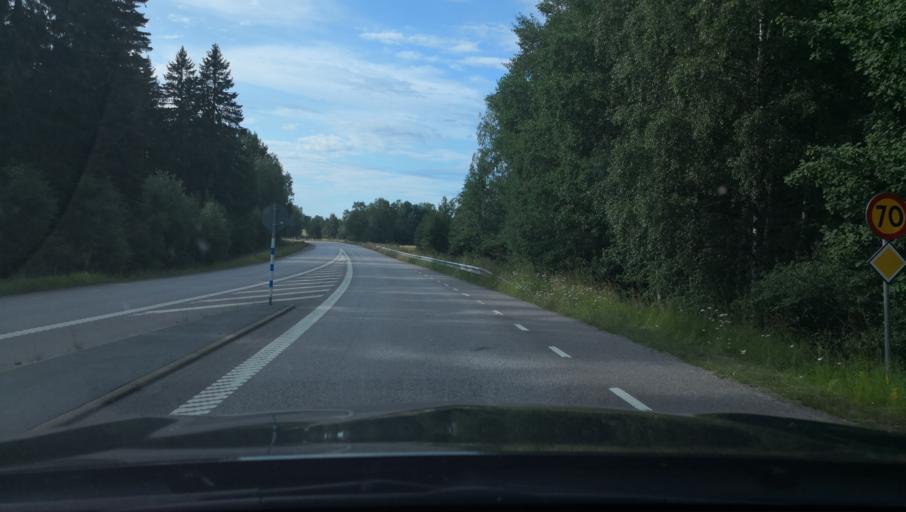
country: SE
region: Uppsala
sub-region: Habo Kommun
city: Balsta
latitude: 59.6053
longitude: 17.5062
